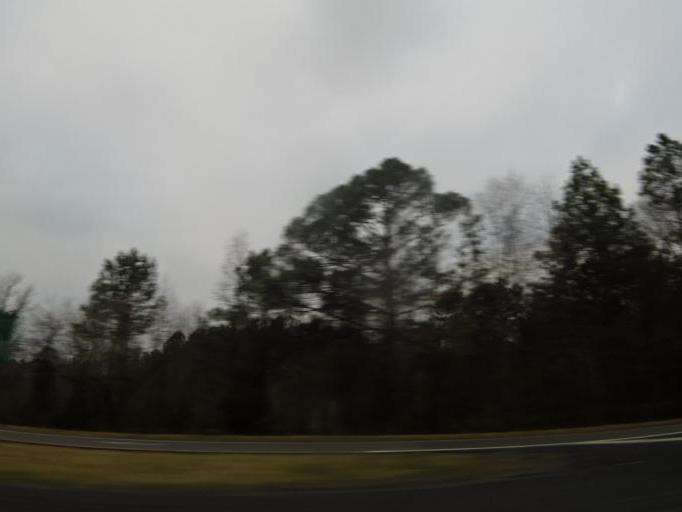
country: US
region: Alabama
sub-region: Blount County
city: Smoke Rise
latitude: 33.9134
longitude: -86.8655
